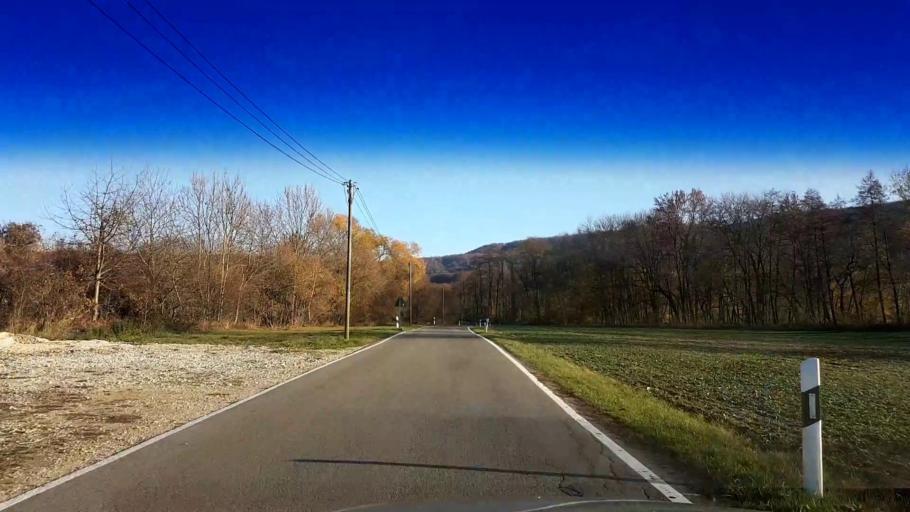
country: DE
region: Bavaria
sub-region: Upper Franconia
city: Schesslitz
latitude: 49.9482
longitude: 11.0412
